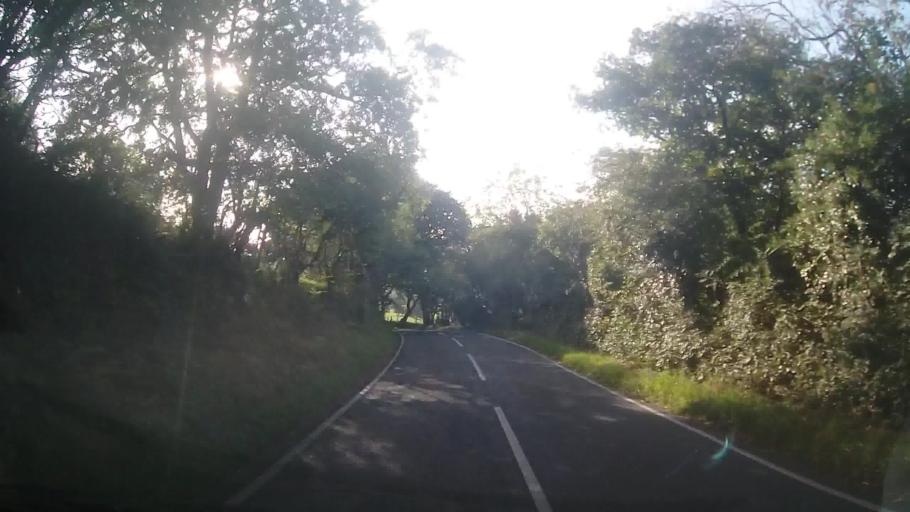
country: GB
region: Wales
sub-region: Pembrokeshire
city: Fishguard
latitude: 51.9773
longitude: -4.9181
